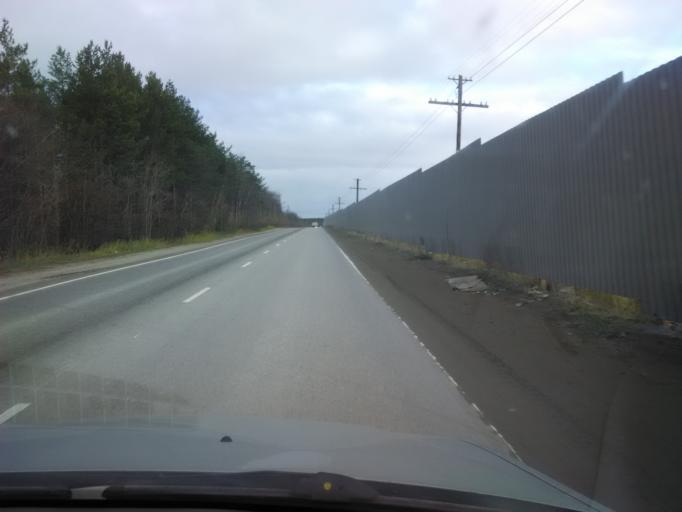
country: RU
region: Murmansk
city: Polyarnyye Zori
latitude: 67.3823
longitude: 32.5110
